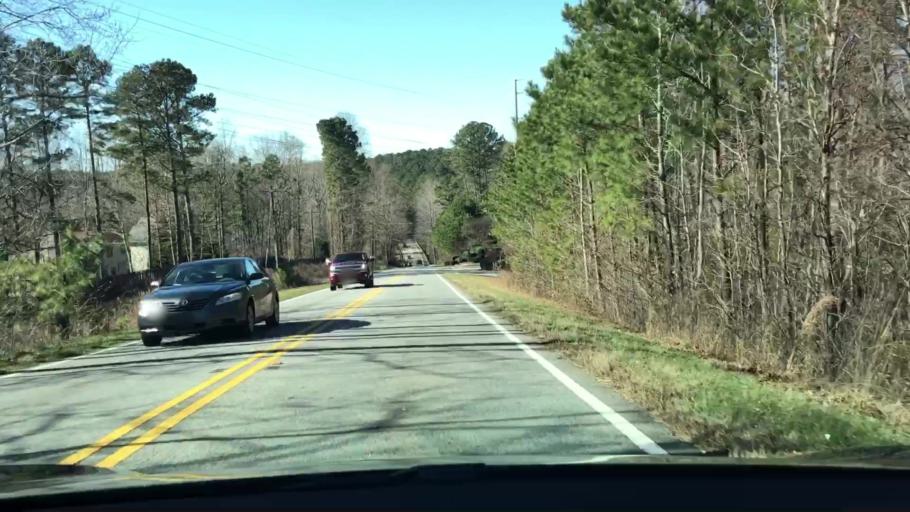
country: US
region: Georgia
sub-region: Forsyth County
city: Cumming
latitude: 34.1856
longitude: -84.1105
